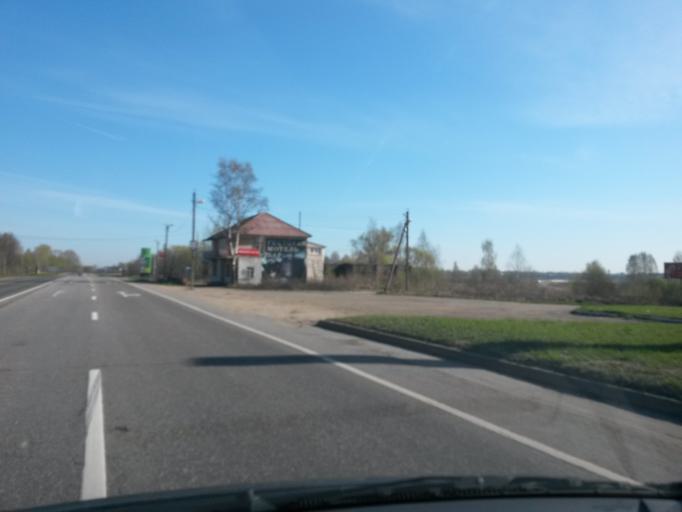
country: RU
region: Jaroslavl
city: Ishnya
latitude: 57.1692
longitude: 39.3582
